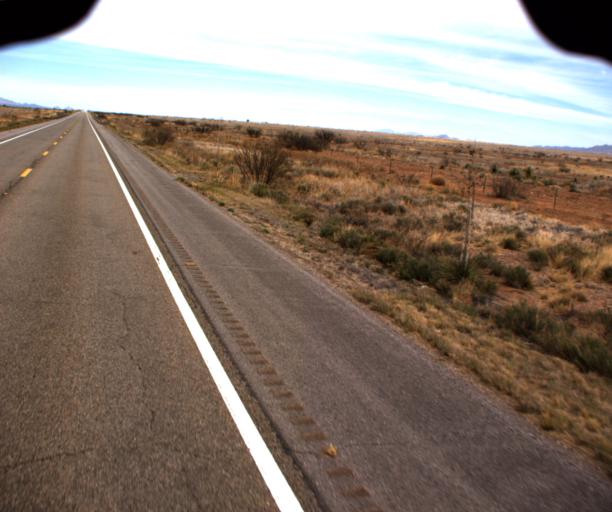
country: US
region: Arizona
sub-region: Cochise County
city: Pirtleville
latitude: 31.5264
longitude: -109.6492
